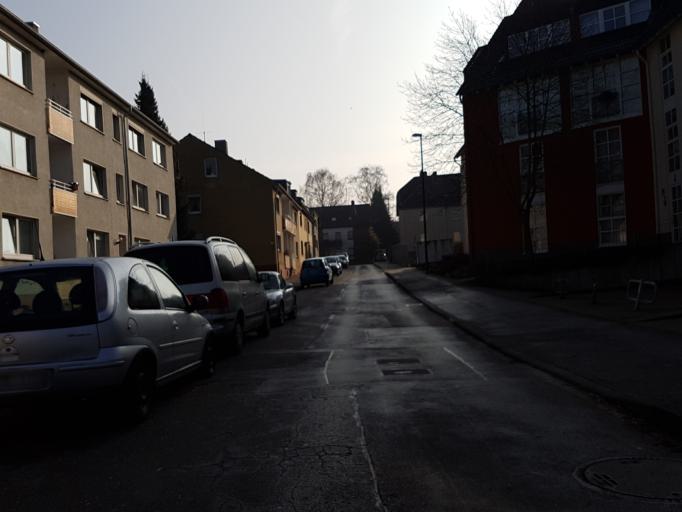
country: DE
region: North Rhine-Westphalia
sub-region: Regierungsbezirk Koln
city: Wurselen
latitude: 50.7947
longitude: 6.1303
